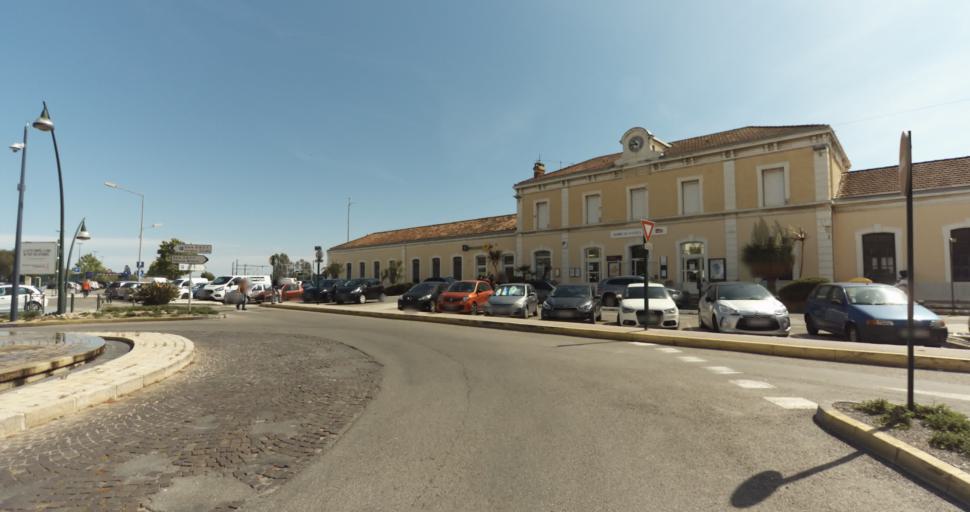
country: FR
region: Provence-Alpes-Cote d'Azur
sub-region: Departement du Var
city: Hyeres
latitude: 43.1092
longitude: 6.1243
